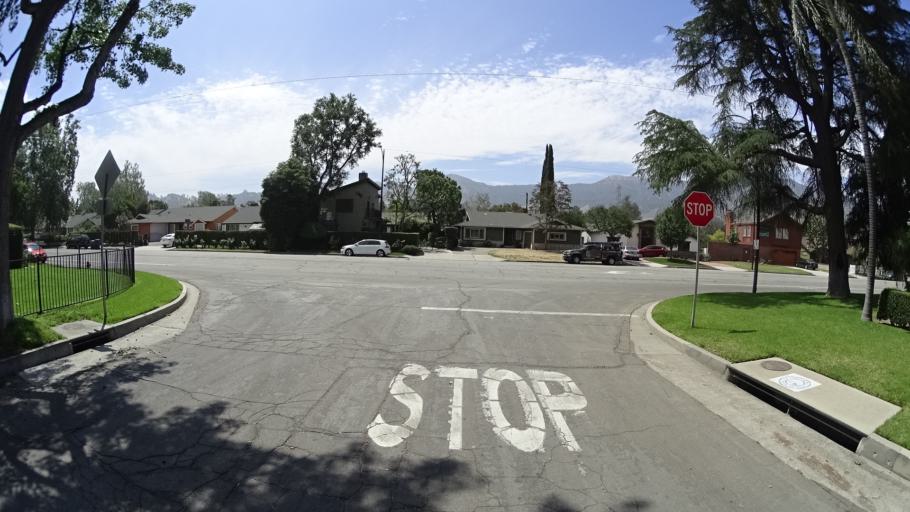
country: US
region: California
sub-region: Los Angeles County
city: Burbank
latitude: 34.1570
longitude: -118.3192
